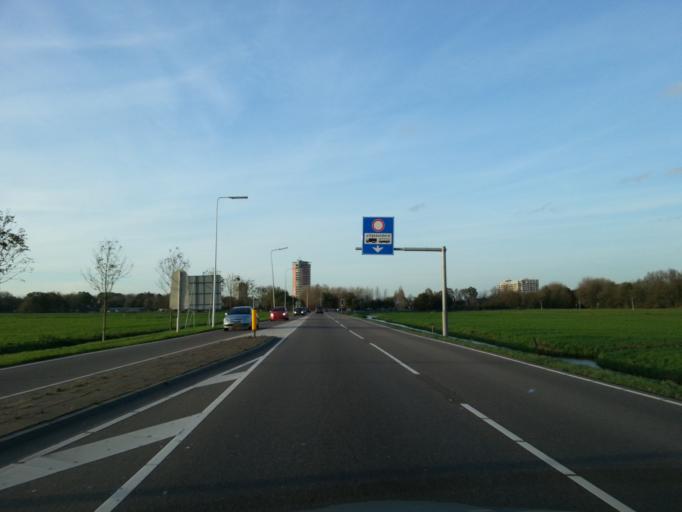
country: NL
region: South Holland
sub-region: Gemeente Leiden
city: Leiden
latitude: 52.1347
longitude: 4.4901
